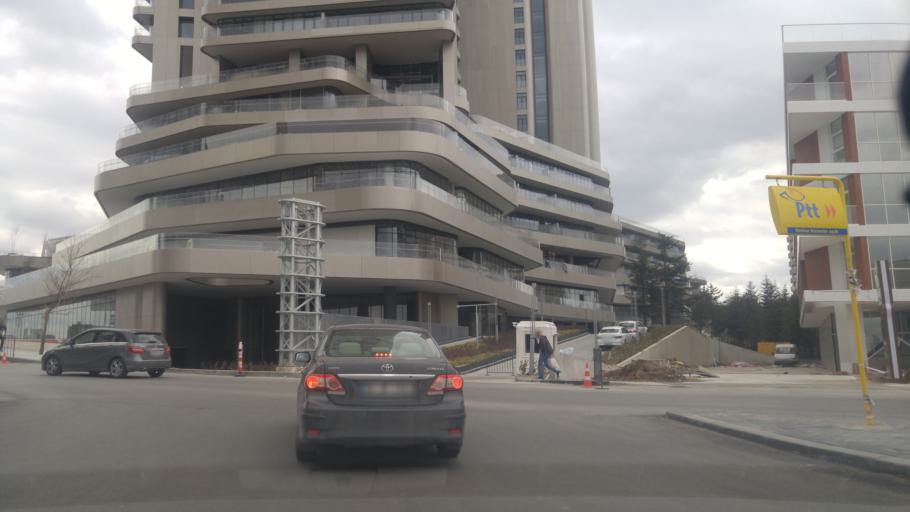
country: TR
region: Ankara
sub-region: Goelbasi
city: Golbasi
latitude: 39.8470
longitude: 32.8287
